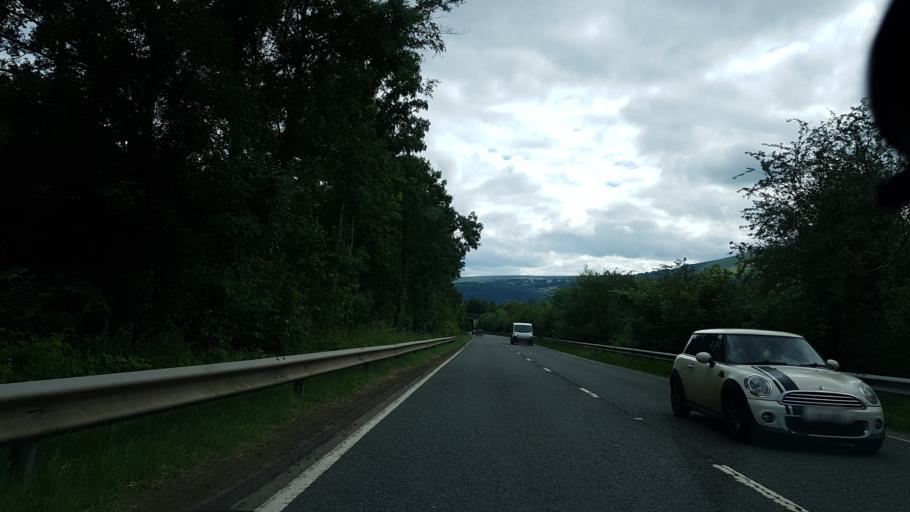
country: GB
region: Wales
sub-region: Monmouthshire
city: Abergavenny
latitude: 51.8264
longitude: -3.0042
